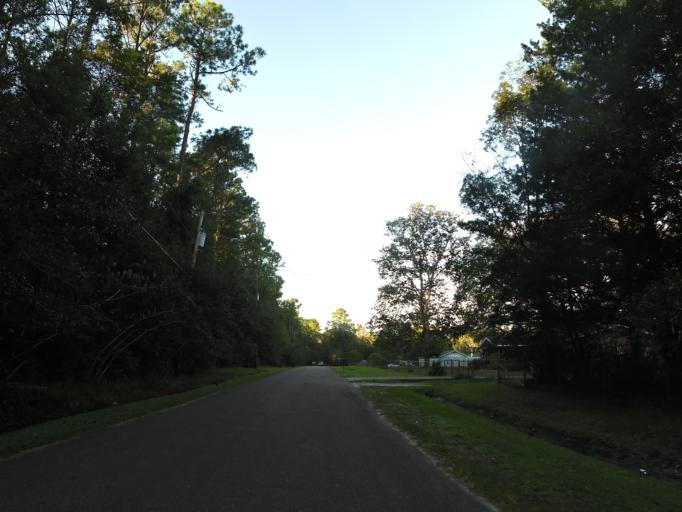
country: US
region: Florida
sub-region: Duval County
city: Jacksonville
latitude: 30.3614
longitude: -81.7646
